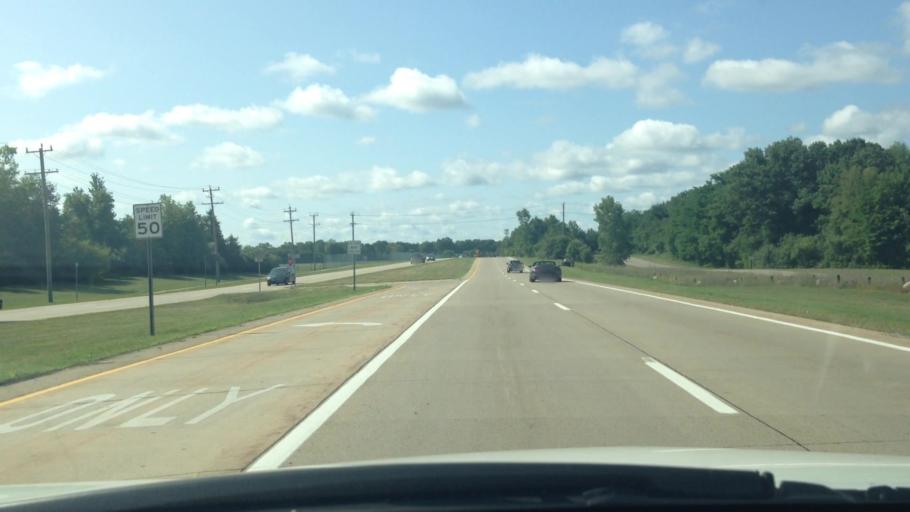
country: US
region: Michigan
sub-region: Oakland County
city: Waterford
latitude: 42.6688
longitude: -83.4388
